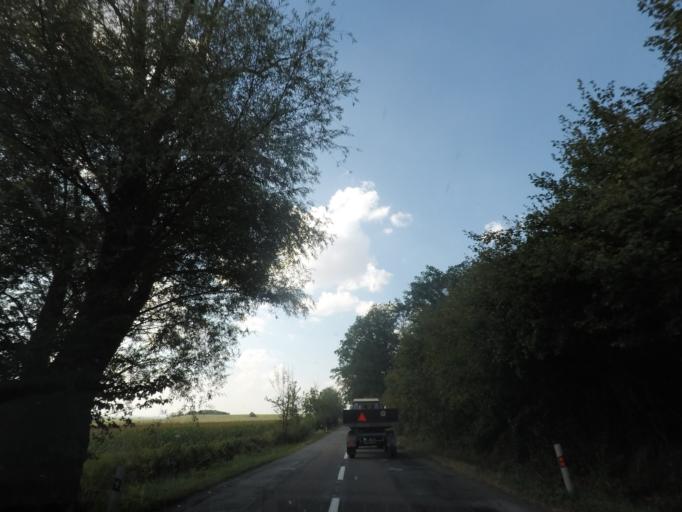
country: CZ
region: Kralovehradecky
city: Trebechovice pod Orebem
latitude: 50.2255
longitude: 15.9725
